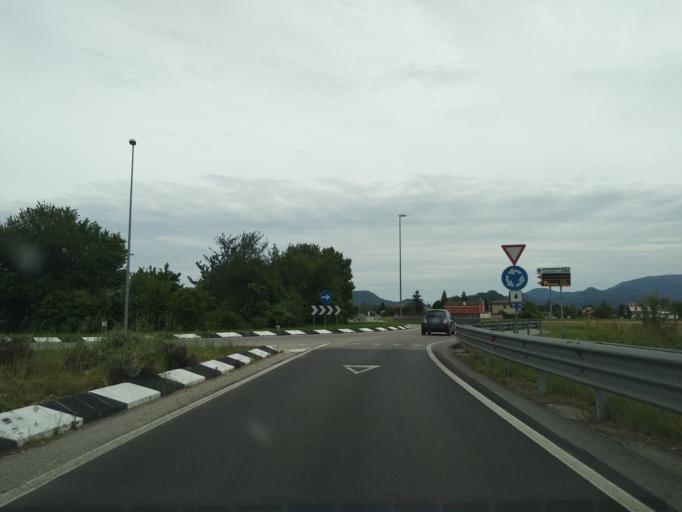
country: IT
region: Veneto
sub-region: Provincia di Padova
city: Montemerlo
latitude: 45.3973
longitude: 11.6969
